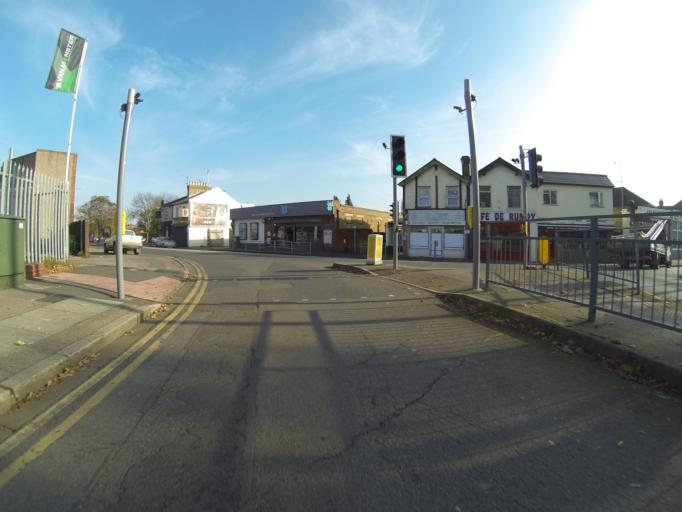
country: GB
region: England
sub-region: Kent
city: Dartford
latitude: 51.4344
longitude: 0.2150
